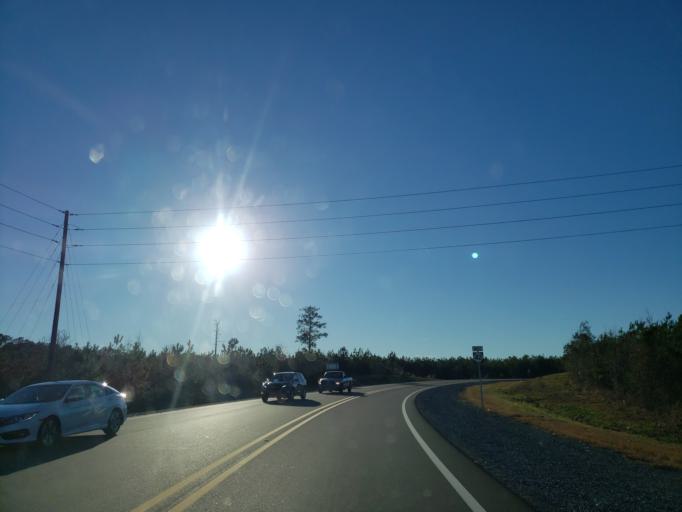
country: US
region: Mississippi
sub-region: Forrest County
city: Rawls Springs
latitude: 31.4190
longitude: -89.4108
